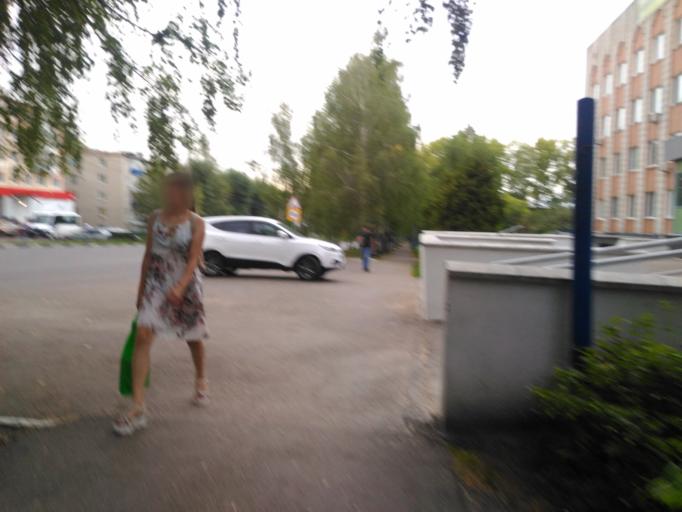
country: RU
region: Ulyanovsk
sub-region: Ulyanovskiy Rayon
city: Ulyanovsk
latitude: 54.2656
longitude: 48.3349
